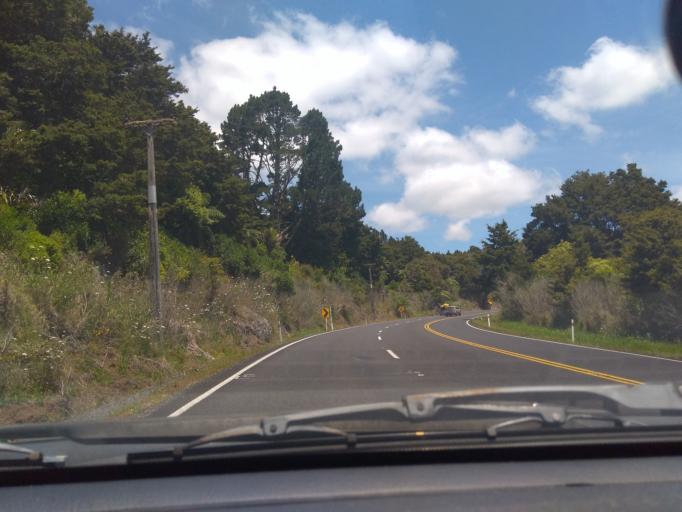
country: NZ
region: Northland
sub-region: Far North District
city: Kerikeri
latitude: -35.1194
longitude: 173.8212
